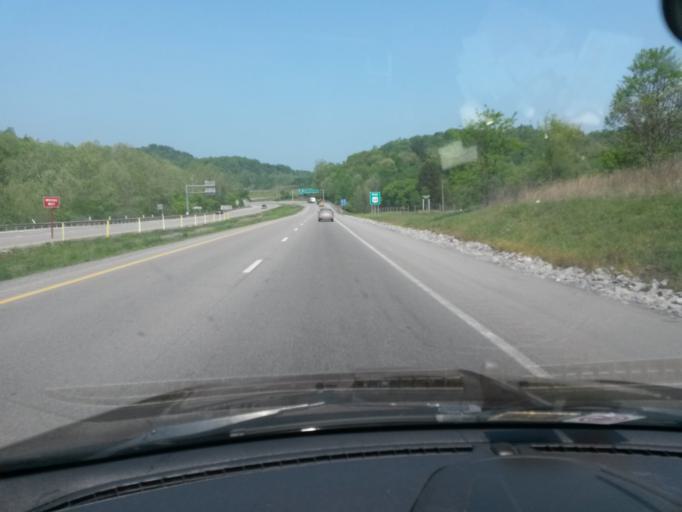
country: US
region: West Virginia
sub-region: Lewis County
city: Weston
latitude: 39.0199
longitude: -80.4199
